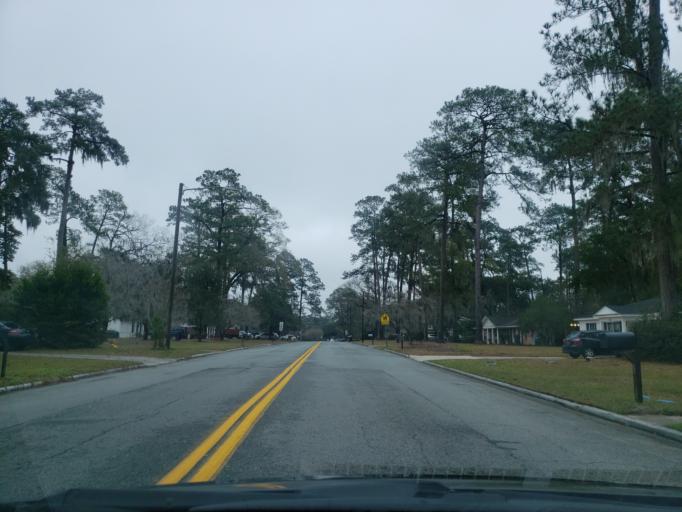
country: US
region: Georgia
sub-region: Chatham County
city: Montgomery
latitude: 31.9727
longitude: -81.1551
